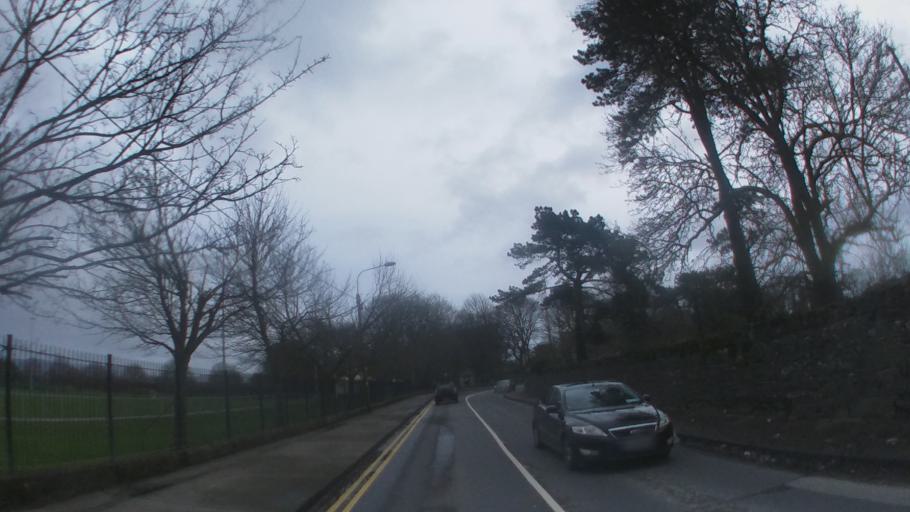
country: IE
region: Leinster
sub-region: Lu
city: Dundalk
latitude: 54.0105
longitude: -6.3960
